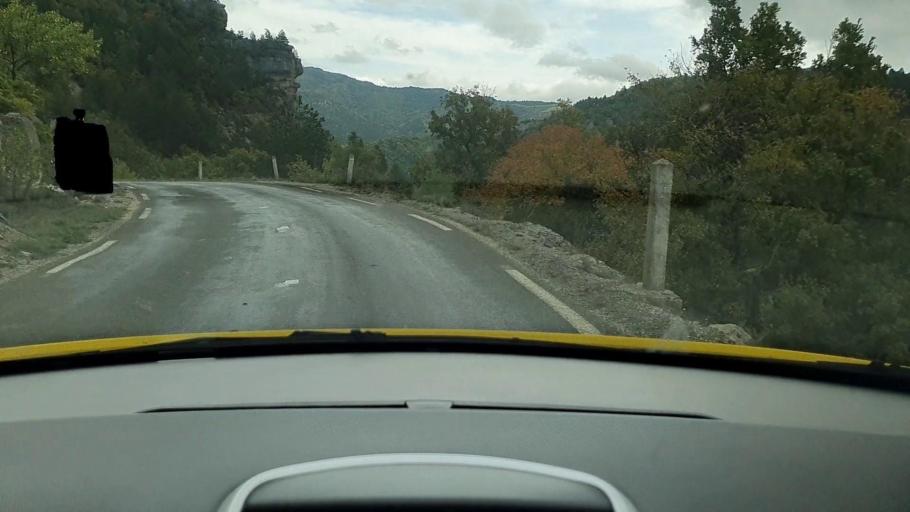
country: FR
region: Languedoc-Roussillon
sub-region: Departement de la Lozere
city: Meyrueis
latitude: 44.0788
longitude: 3.3600
